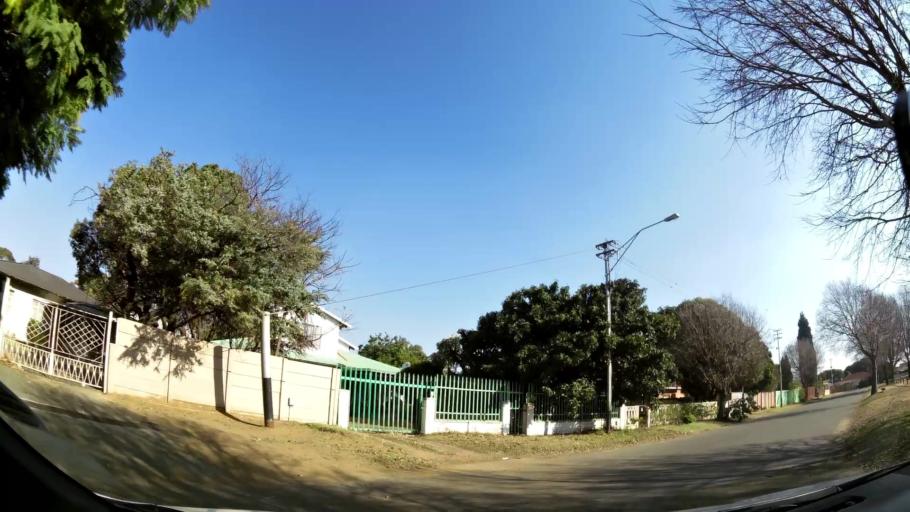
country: ZA
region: Gauteng
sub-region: City of Johannesburg Metropolitan Municipality
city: Johannesburg
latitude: -26.2553
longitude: 28.0055
